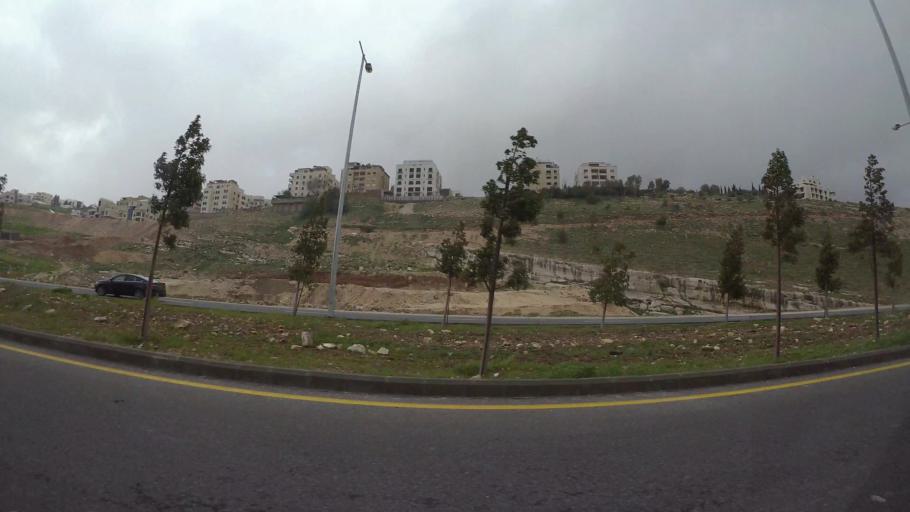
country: JO
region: Amman
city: Al Bunayyat ash Shamaliyah
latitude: 31.9316
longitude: 35.8893
